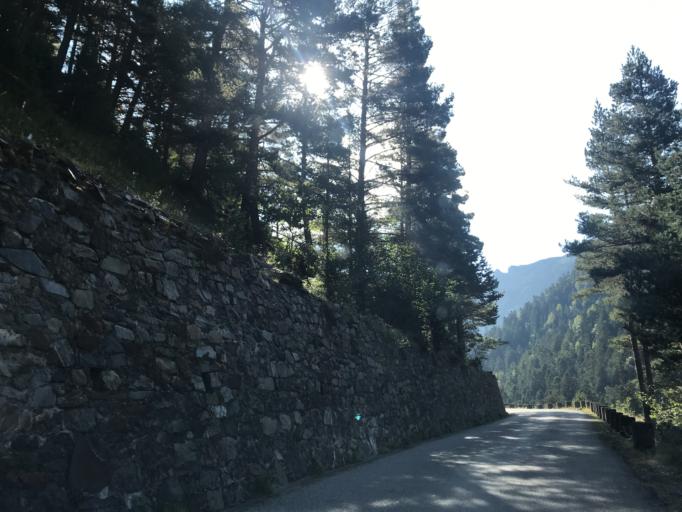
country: FR
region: Midi-Pyrenees
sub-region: Departement des Hautes-Pyrenees
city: Saint-Lary-Soulan
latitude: 42.8214
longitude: 0.1845
